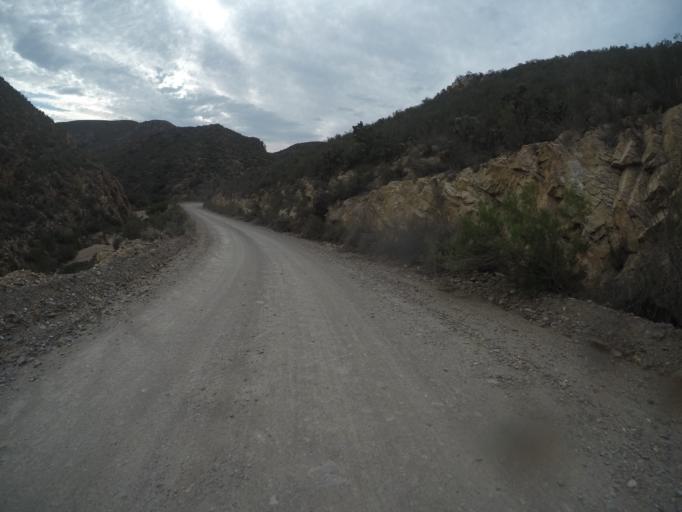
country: ZA
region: Eastern Cape
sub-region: Cacadu District Municipality
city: Willowmore
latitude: -33.5068
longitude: 23.6359
